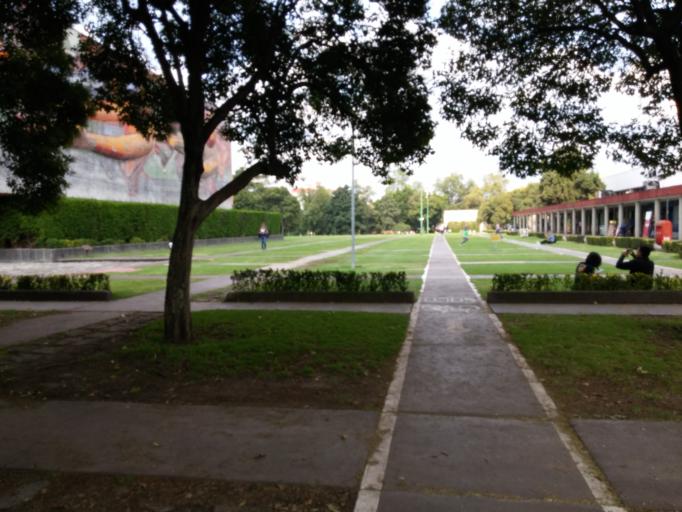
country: MX
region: Mexico City
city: Magdalena Contreras
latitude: 19.3316
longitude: -99.1886
